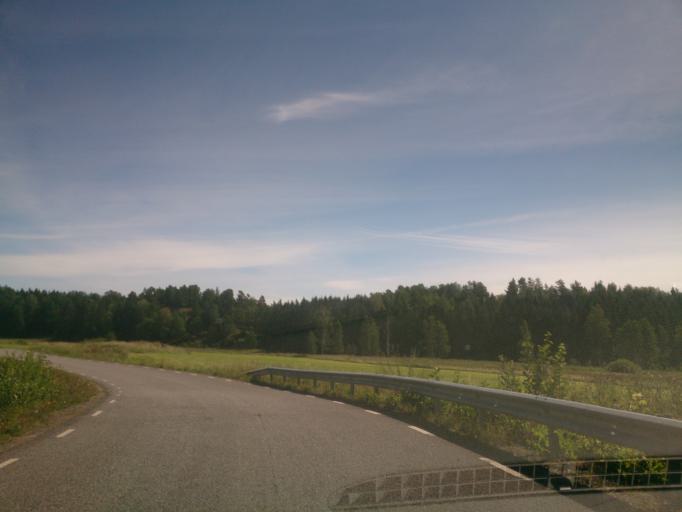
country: SE
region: OEstergoetland
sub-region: Valdemarsviks Kommun
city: Valdemarsvik
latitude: 58.2761
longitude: 16.6961
